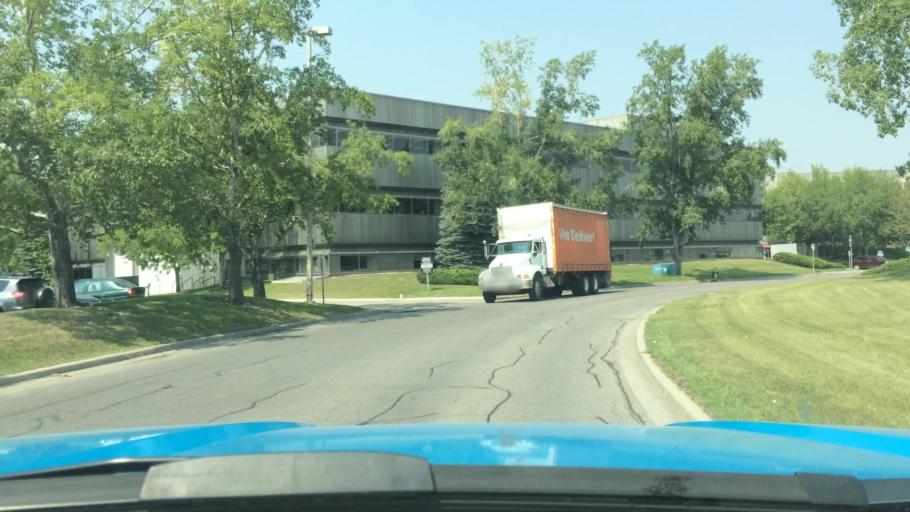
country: CA
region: Alberta
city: Calgary
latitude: 51.1124
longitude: -114.0442
